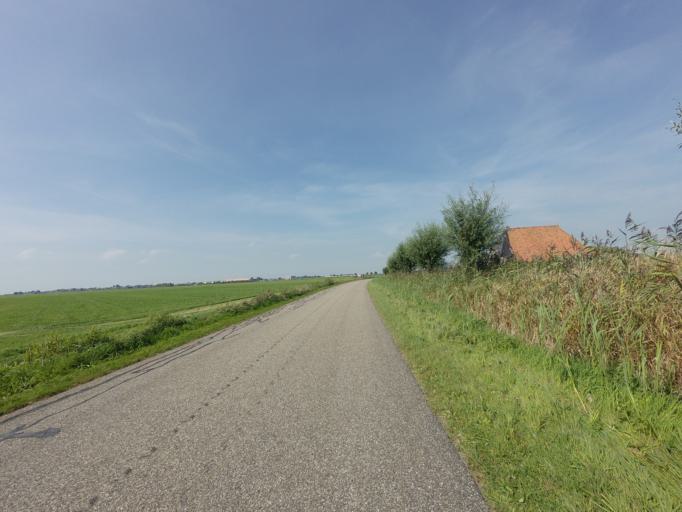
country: NL
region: Friesland
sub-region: Sudwest Fryslan
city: Woudsend
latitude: 52.9369
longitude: 5.6573
